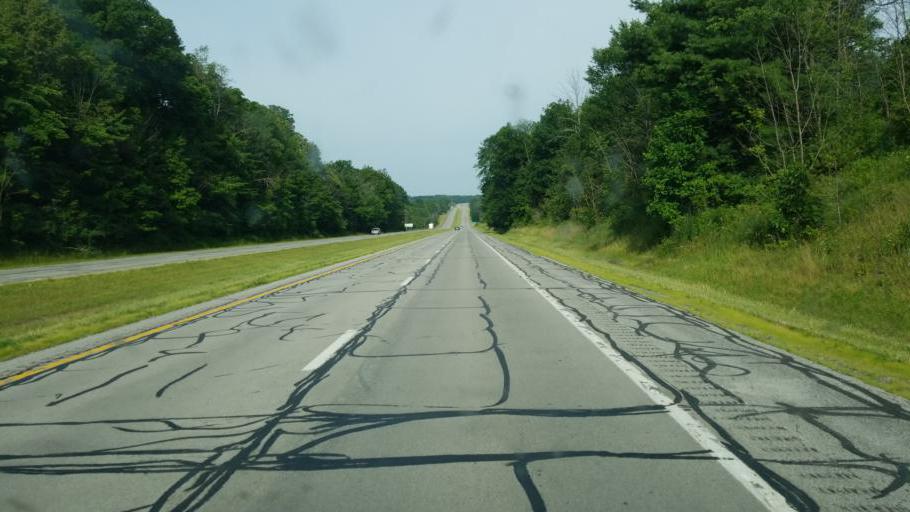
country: US
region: Ohio
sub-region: Medina County
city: Westfield Center
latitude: 41.0390
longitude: -81.9469
